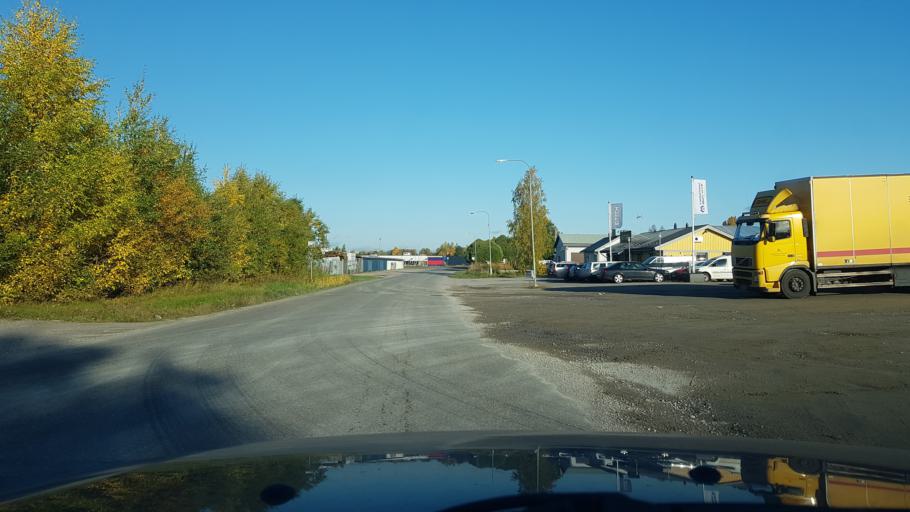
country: SE
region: Norrbotten
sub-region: Pitea Kommun
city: Bergsviken
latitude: 65.3388
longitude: 21.4115
